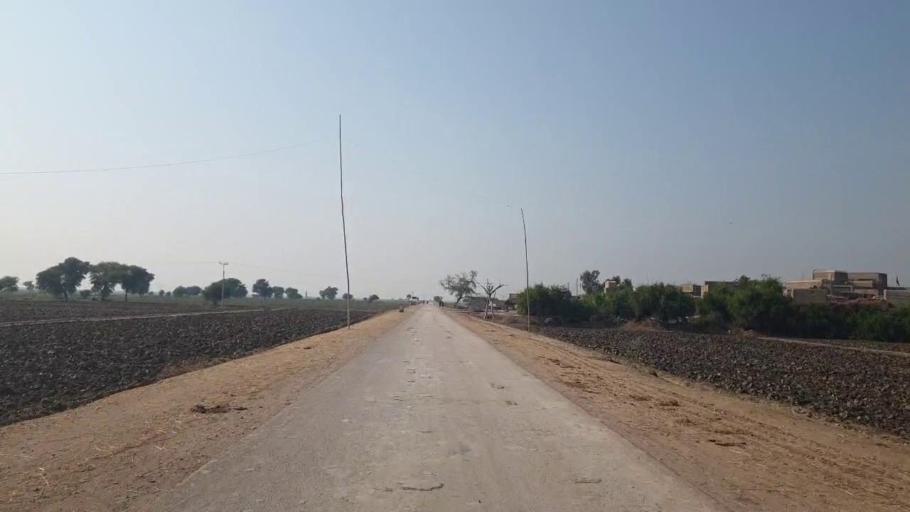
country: PK
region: Sindh
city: Sehwan
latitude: 26.4236
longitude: 67.8303
